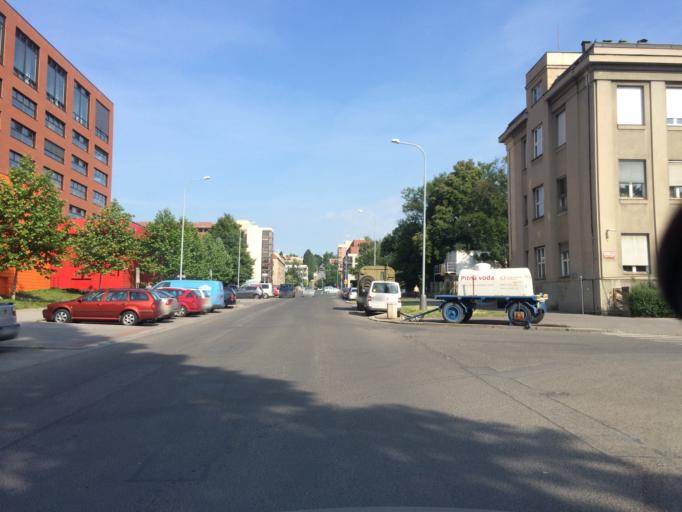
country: CZ
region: Praha
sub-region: Praha 1
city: Mala Strana
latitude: 50.1050
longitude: 14.3910
